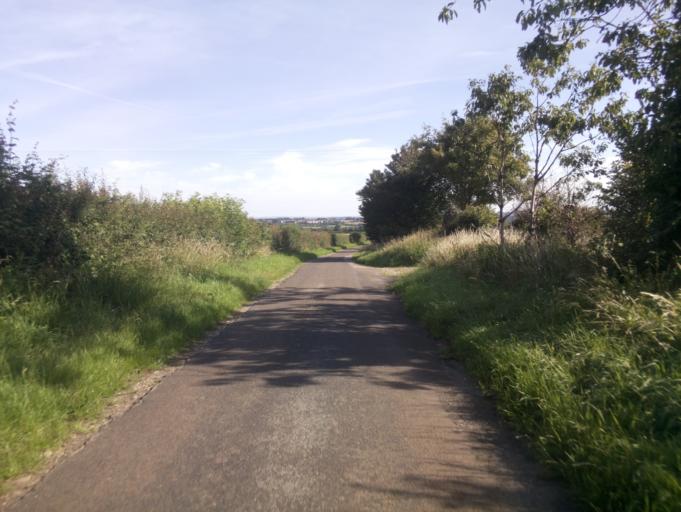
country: GB
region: England
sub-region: Bath and North East Somerset
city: Publow
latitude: 51.3926
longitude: -2.5328
